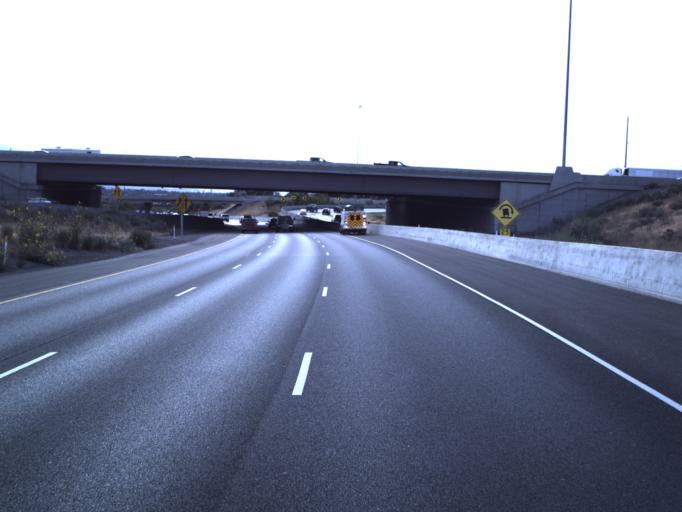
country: US
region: Utah
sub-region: Salt Lake County
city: Midvale
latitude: 40.6360
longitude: -111.9031
